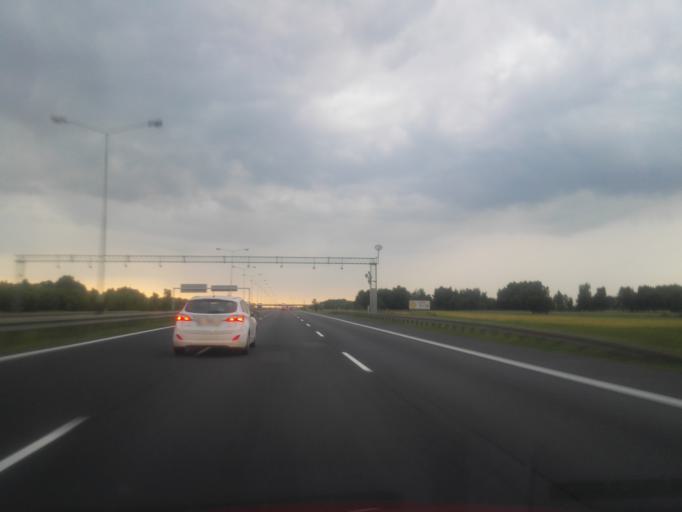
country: PL
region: Lodz Voivodeship
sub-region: Piotrkow Trybunalski
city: Piotrkow Trybunalski
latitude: 51.4209
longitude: 19.6383
